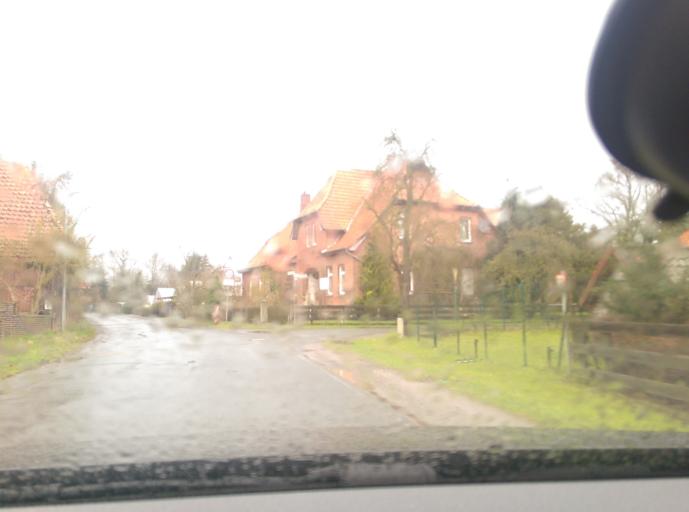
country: DE
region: Lower Saxony
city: Schwarmstedt
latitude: 52.6344
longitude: 9.6074
